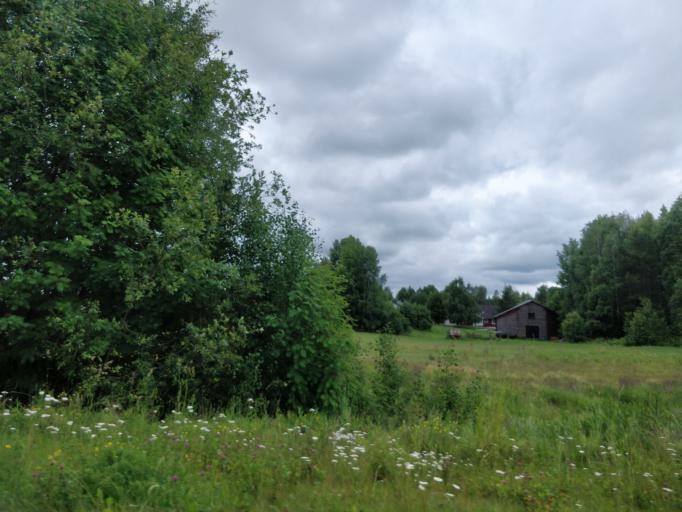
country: SE
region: Vaesterbotten
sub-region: Skelleftea Kommun
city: Viken
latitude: 64.7576
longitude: 20.8979
